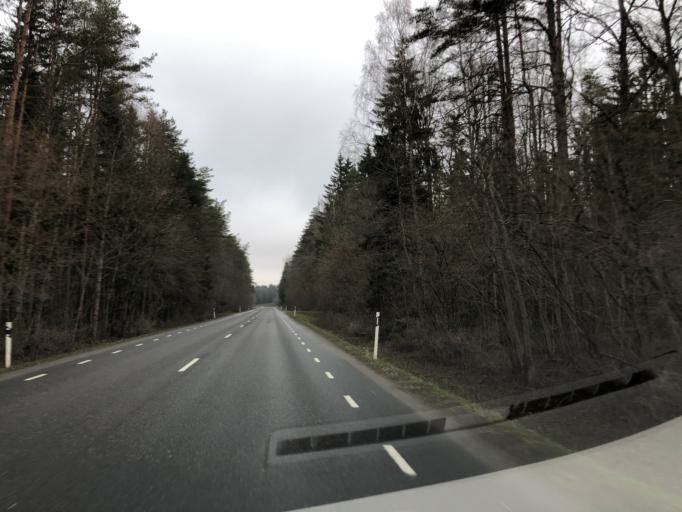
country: EE
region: Laeaene-Virumaa
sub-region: Vaeike-Maarja vald
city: Vaike-Maarja
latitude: 59.0802
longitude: 26.2397
